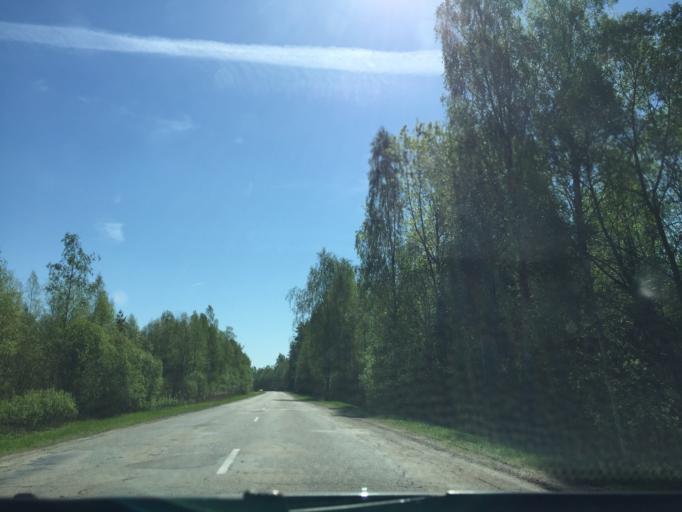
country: LV
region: Incukalns
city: Incukalns
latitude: 57.0260
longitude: 24.7490
